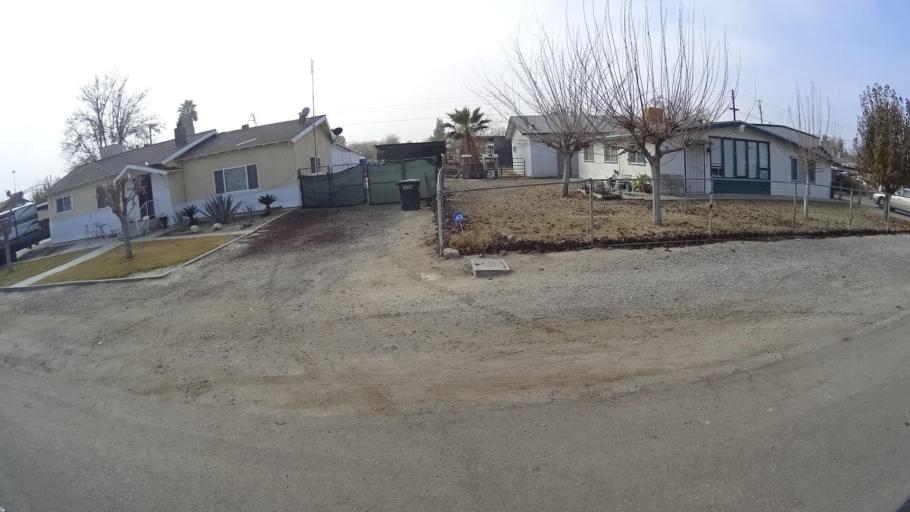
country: US
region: California
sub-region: Kern County
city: Ford City
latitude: 35.2053
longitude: -119.4061
